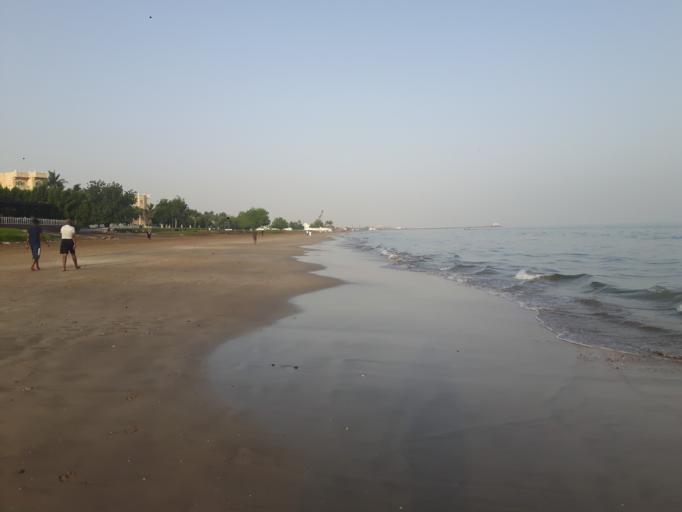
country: OM
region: Muhafazat Masqat
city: Bawshar
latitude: 23.6108
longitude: 58.4458
